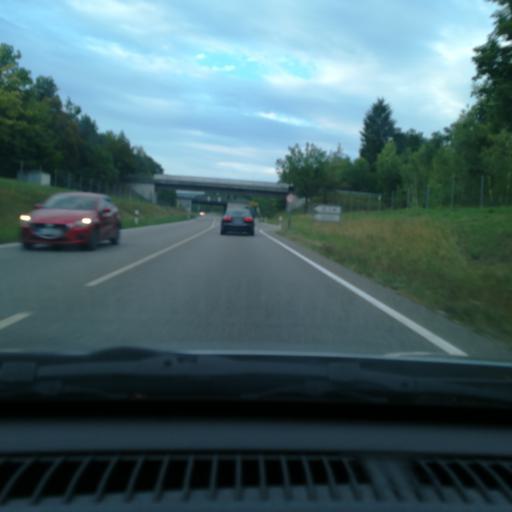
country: DE
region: Baden-Wuerttemberg
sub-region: Freiburg Region
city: Steisslingen
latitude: 47.7680
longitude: 8.9130
